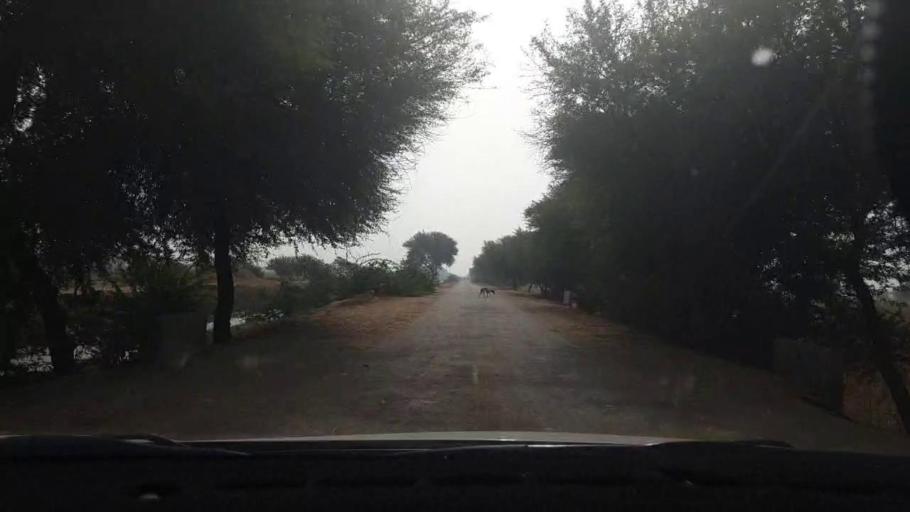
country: PK
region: Sindh
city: Tando Muhammad Khan
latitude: 25.0647
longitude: 68.5414
